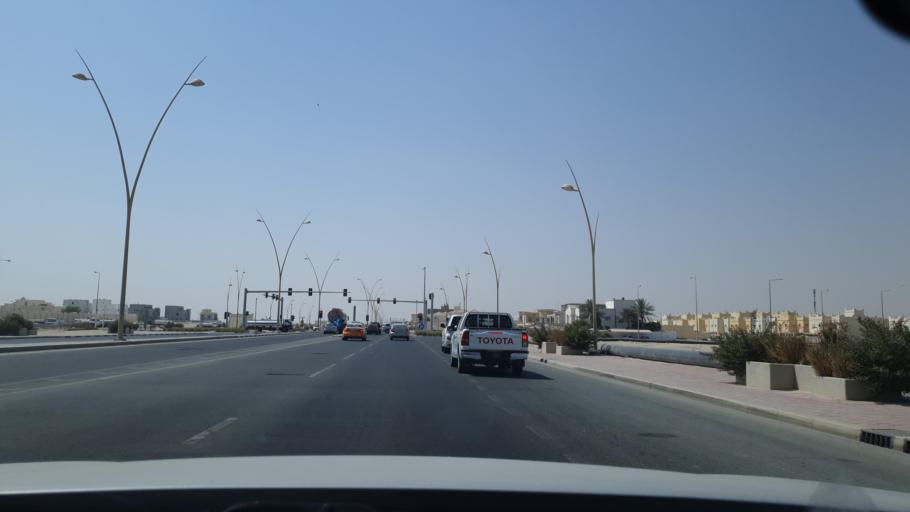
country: QA
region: Al Khawr
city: Al Khawr
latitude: 25.6760
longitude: 51.4902
